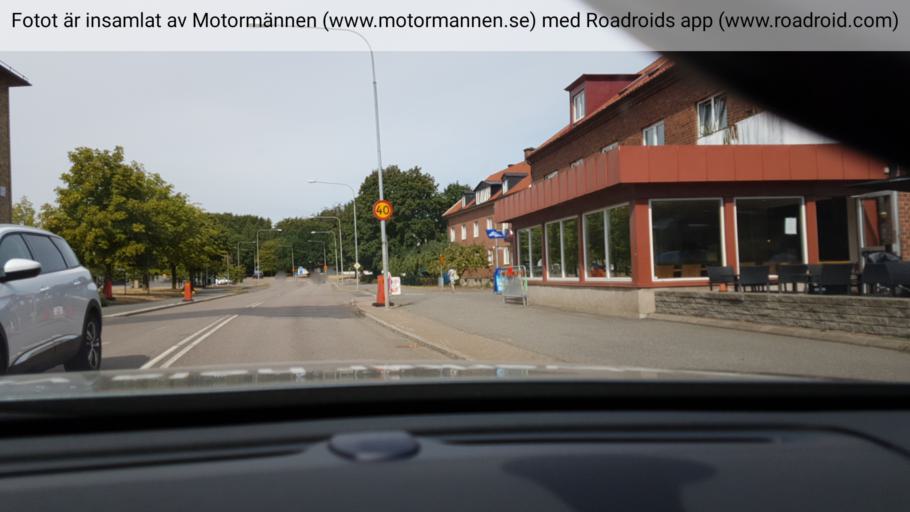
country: SE
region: Vaestra Goetaland
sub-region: Skovde Kommun
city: Skoevde
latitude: 58.3864
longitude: 13.8582
